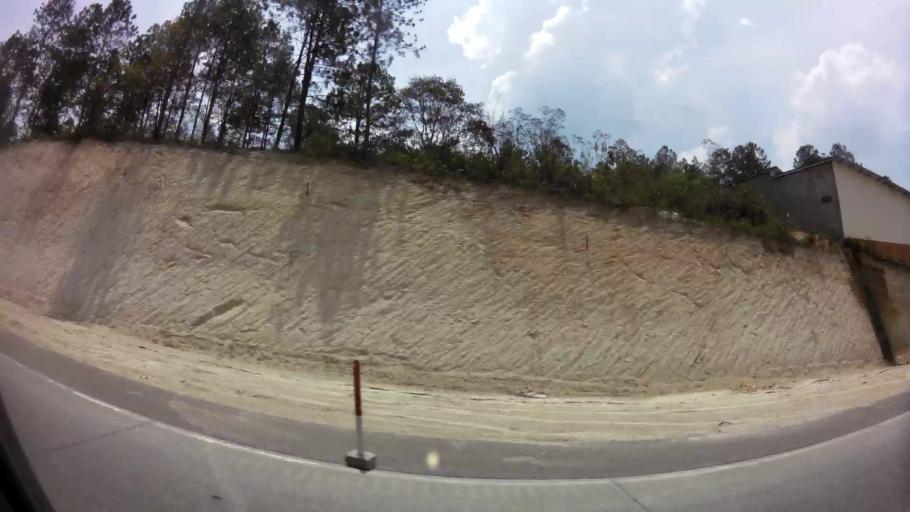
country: HN
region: Comayagua
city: El Socorro
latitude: 14.6345
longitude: -87.9218
